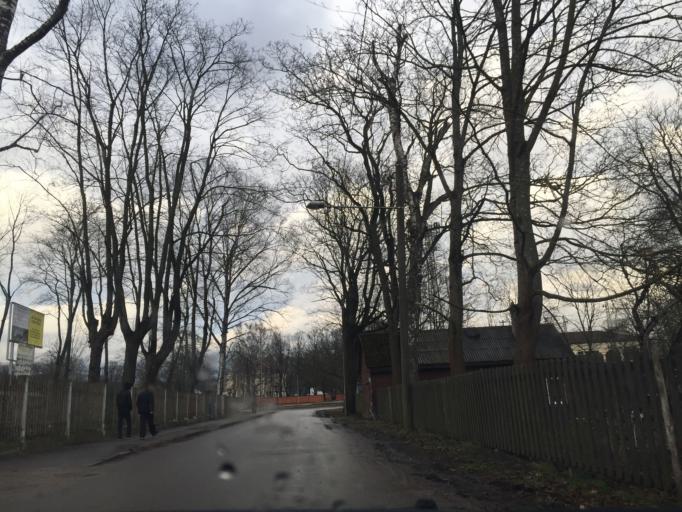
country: LV
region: Marupe
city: Marupe
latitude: 56.9415
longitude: 24.0496
